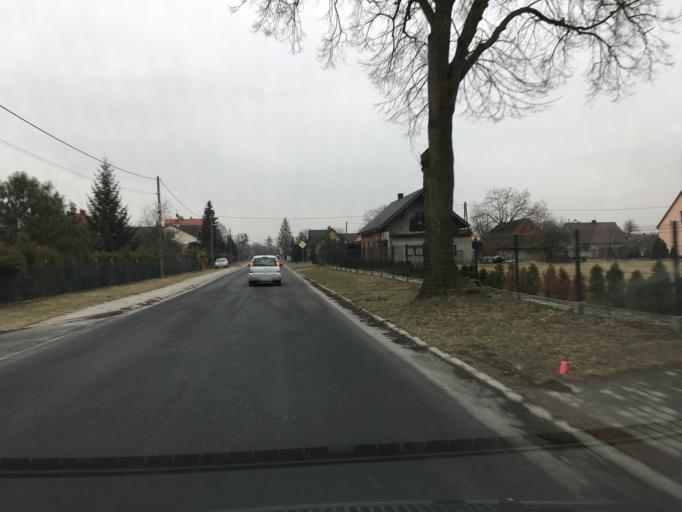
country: PL
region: Opole Voivodeship
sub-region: Powiat kedzierzynsko-kozielski
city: Bierawa
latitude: 50.2868
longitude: 18.2380
